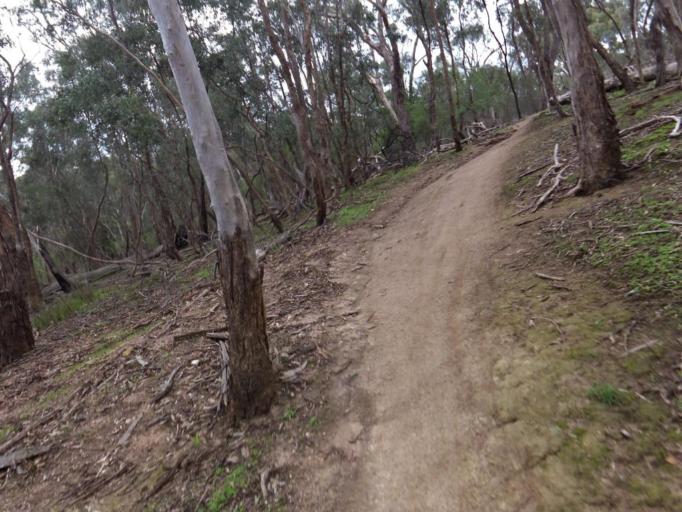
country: AU
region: Victoria
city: Plenty
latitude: -37.6775
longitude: 145.0955
